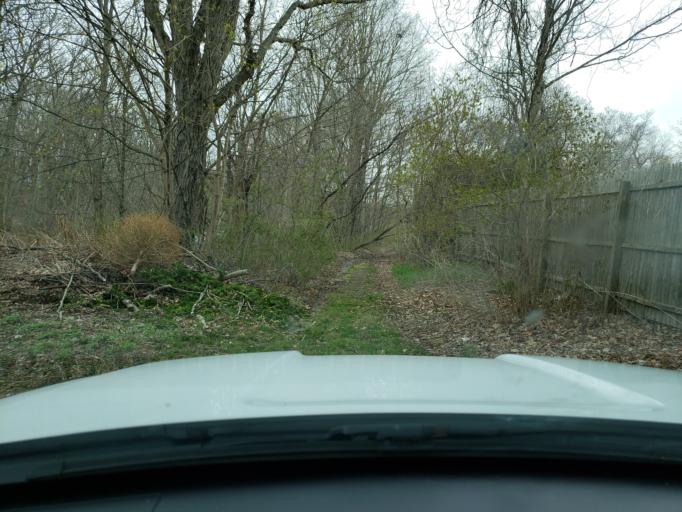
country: US
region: Connecticut
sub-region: Windham County
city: Wauregan
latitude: 41.7220
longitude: -71.9083
